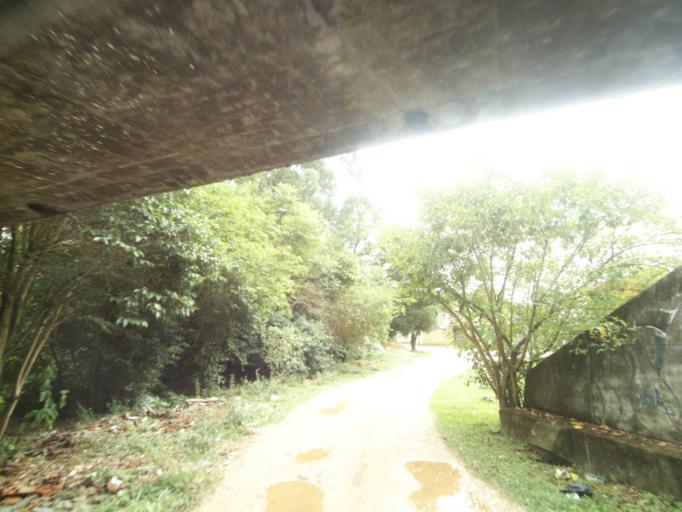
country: BR
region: Parana
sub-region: Curitiba
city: Curitiba
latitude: -25.4348
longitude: -49.3145
